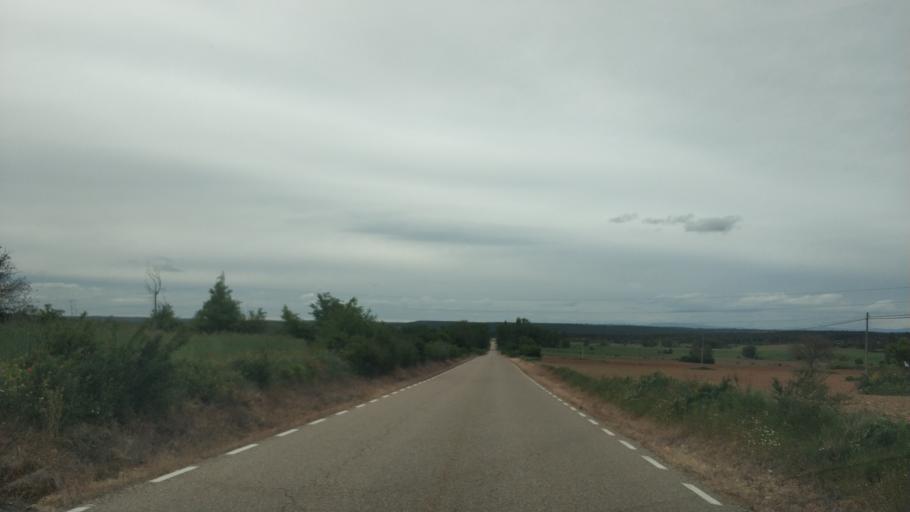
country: ES
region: Castille and Leon
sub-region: Provincia de Soria
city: Berlanga de Duero
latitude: 41.4835
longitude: -2.8652
